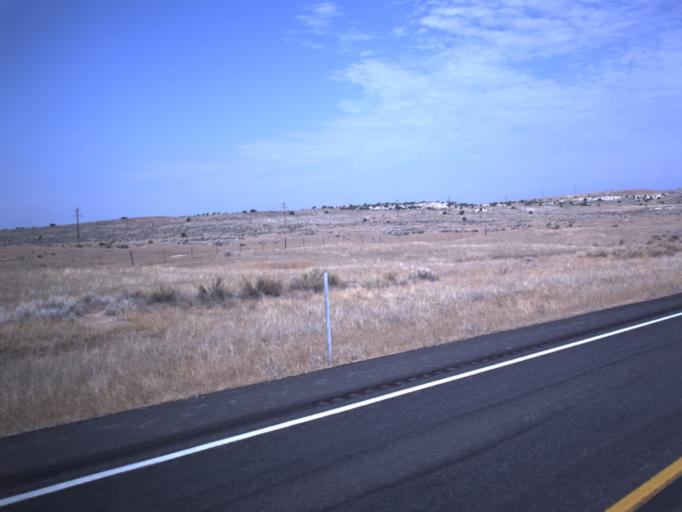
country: US
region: Utah
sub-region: Uintah County
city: Naples
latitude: 40.3432
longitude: -109.2994
